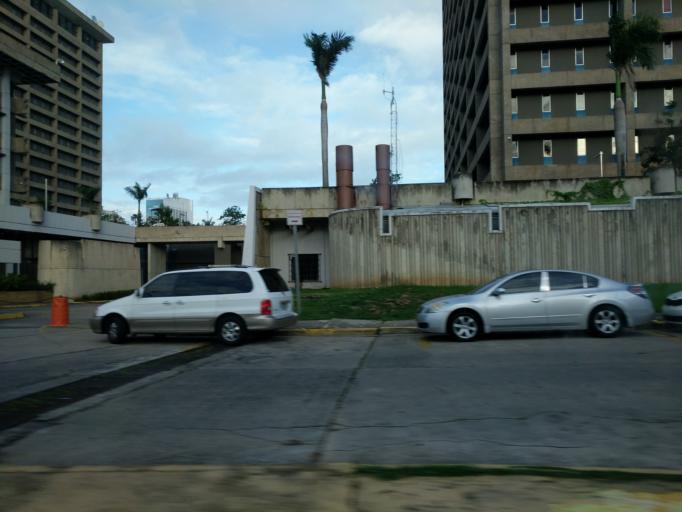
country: PR
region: San Juan
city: San Juan
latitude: 18.4488
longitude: -66.0681
